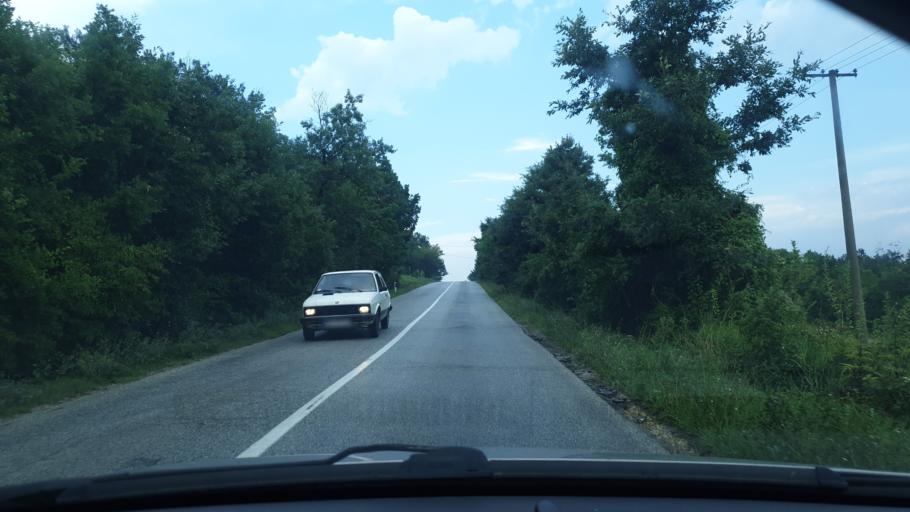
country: RS
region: Central Serbia
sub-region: Sumadijski Okrug
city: Kragujevac
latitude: 44.0441
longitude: 20.7934
